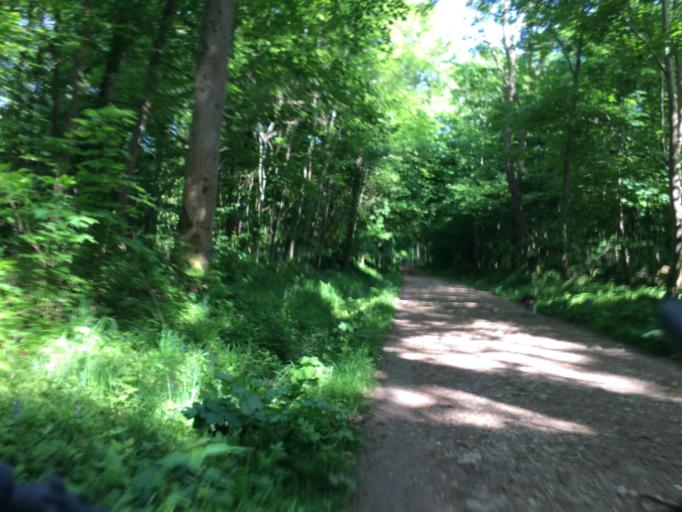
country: FR
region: Ile-de-France
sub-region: Departement des Hauts-de-Seine
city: Chatenay-Malabry
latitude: 48.7588
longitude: 2.2483
